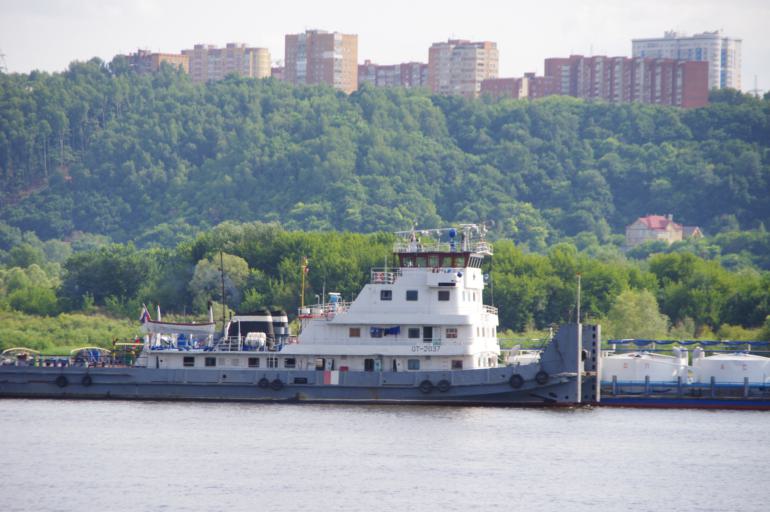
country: RU
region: Nizjnij Novgorod
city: Bor
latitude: 56.3355
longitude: 44.0820
